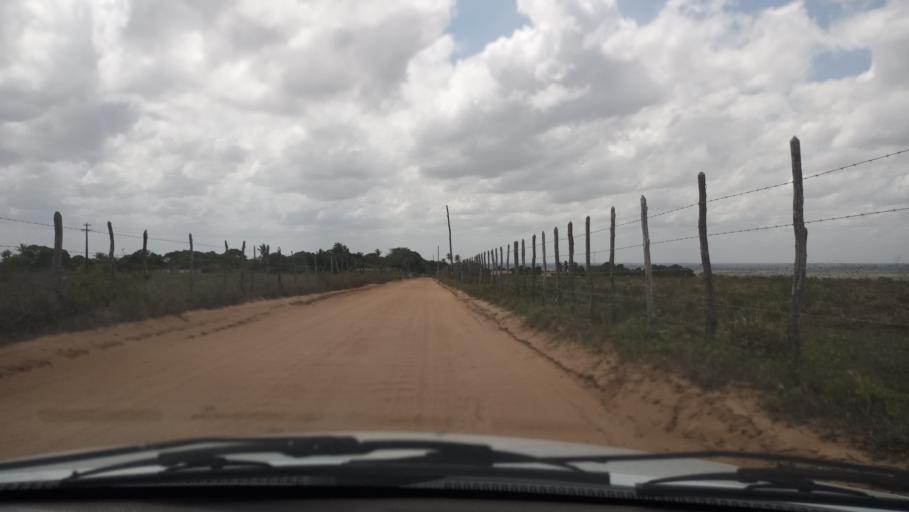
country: BR
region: Rio Grande do Norte
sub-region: Montanhas
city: Montanhas
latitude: -6.3611
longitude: -35.3341
